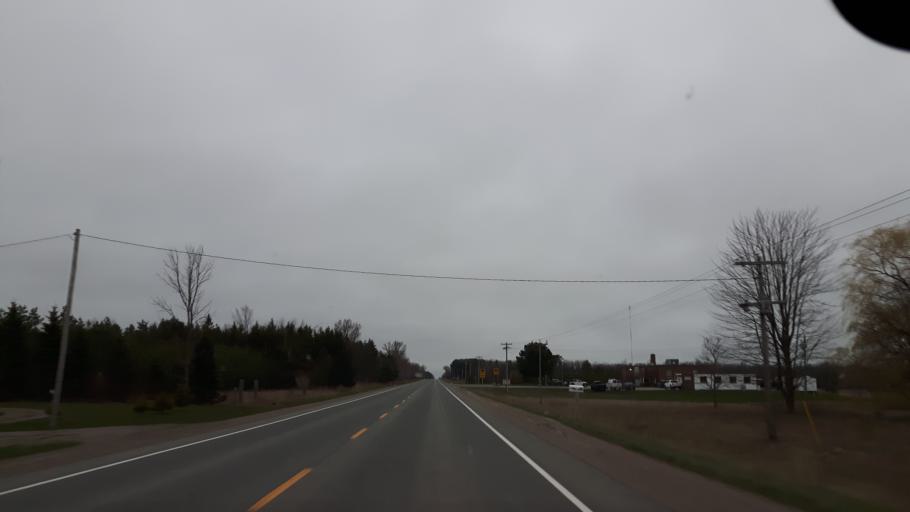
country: CA
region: Ontario
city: Goderich
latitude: 43.6897
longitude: -81.7057
